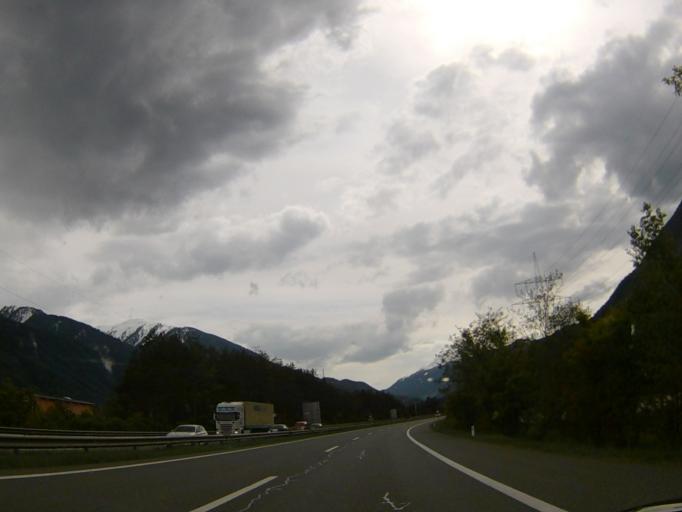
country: AT
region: Tyrol
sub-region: Politischer Bezirk Imst
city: Roppen
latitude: 47.2338
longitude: 10.8359
